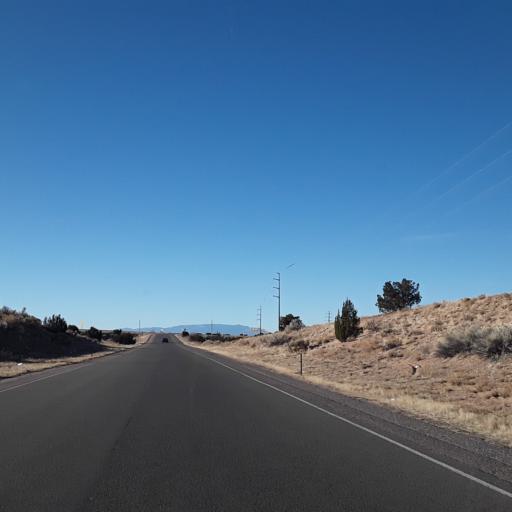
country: US
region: New Mexico
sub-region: Santa Fe County
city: Santa Fe
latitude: 35.6365
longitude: -105.9579
